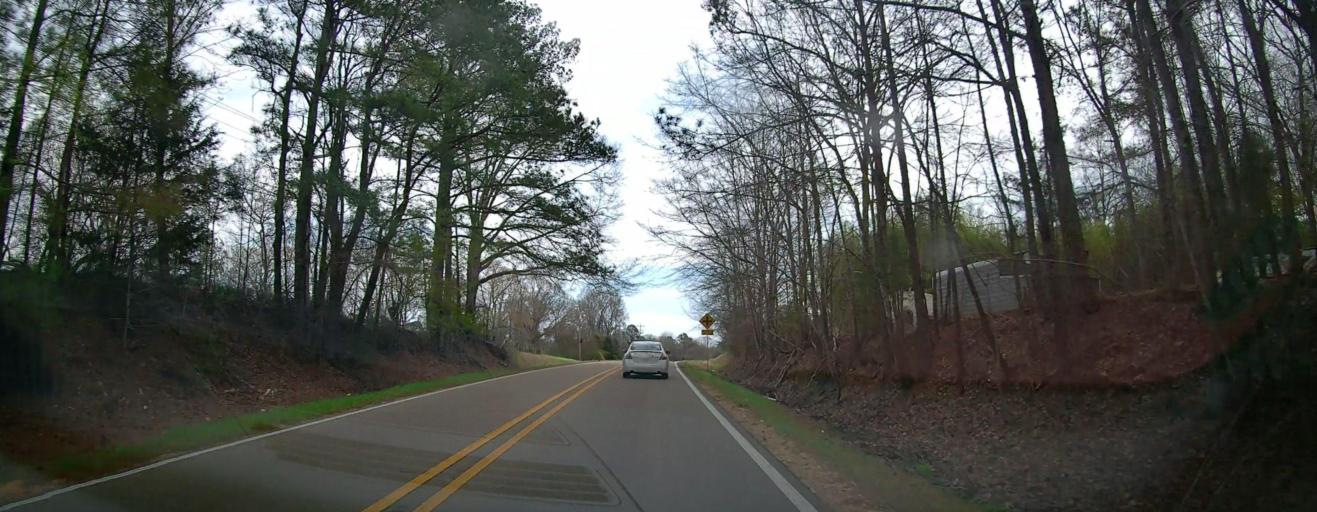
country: US
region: Mississippi
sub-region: Itawamba County
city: Fulton
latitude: 34.2737
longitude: -88.3445
